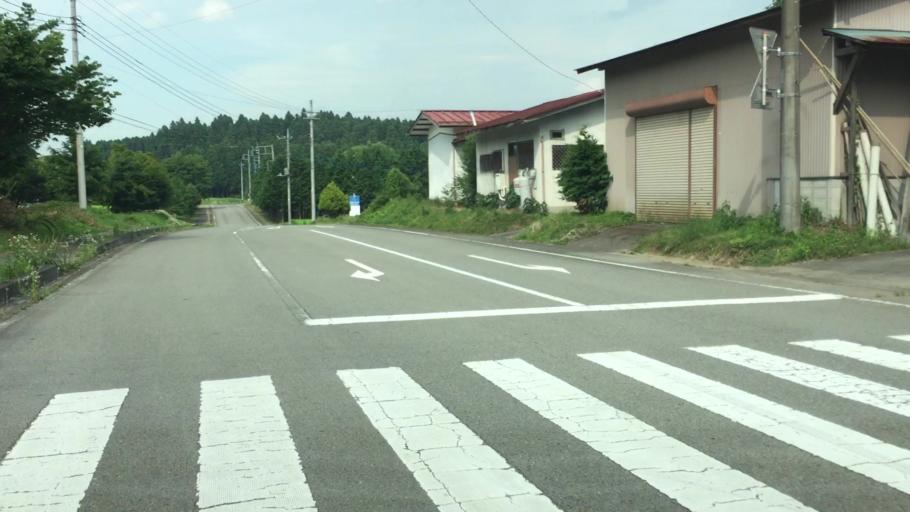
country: JP
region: Tochigi
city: Kuroiso
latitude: 36.9609
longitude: 139.9819
